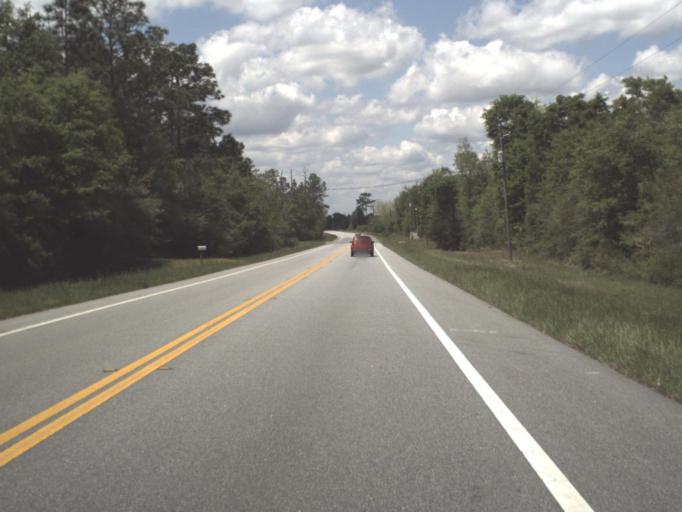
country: US
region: Florida
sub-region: Escambia County
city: Molino
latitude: 30.7851
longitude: -87.4069
